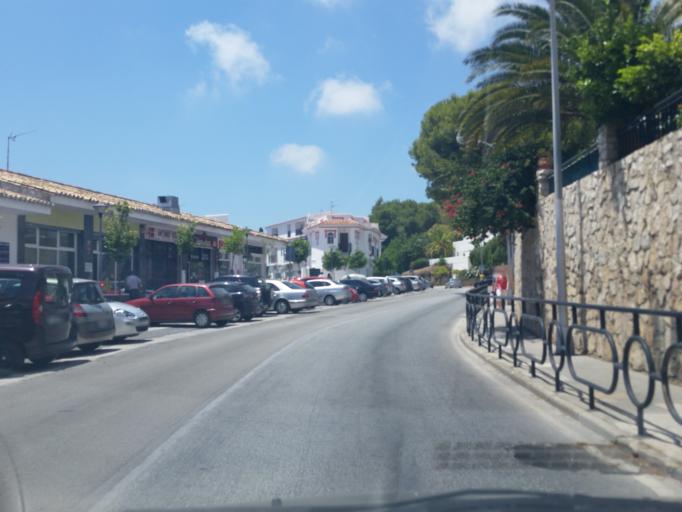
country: ES
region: Andalusia
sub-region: Provincia de Malaga
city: Benalmadena
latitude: 36.5983
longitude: -4.5704
